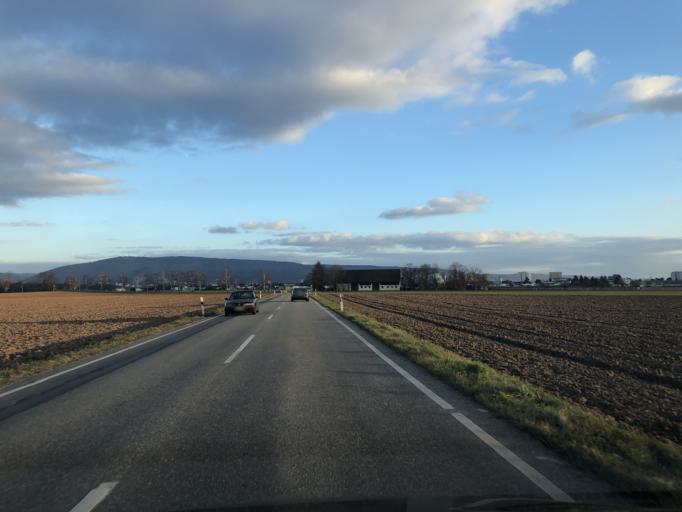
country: DE
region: Baden-Wuerttemberg
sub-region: Karlsruhe Region
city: Eppelheim
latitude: 49.4173
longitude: 8.6178
